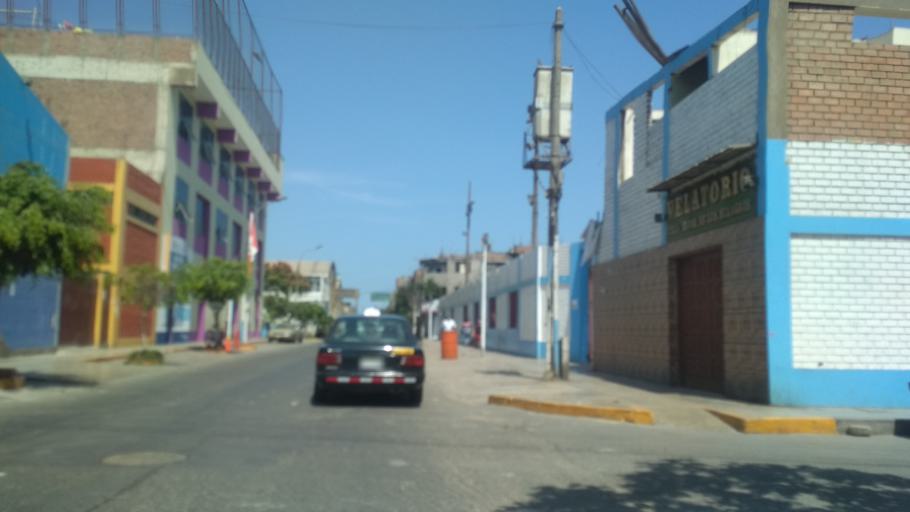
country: PE
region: Callao
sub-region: Callao
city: Callao
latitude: -12.0413
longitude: -77.0860
